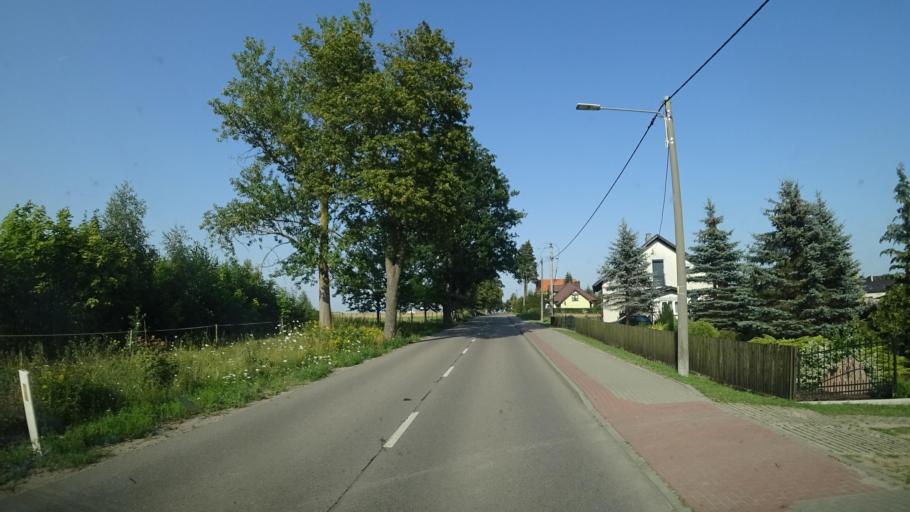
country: PL
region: Pomeranian Voivodeship
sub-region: Powiat czluchowski
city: Przechlewo
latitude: 53.8012
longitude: 17.2664
